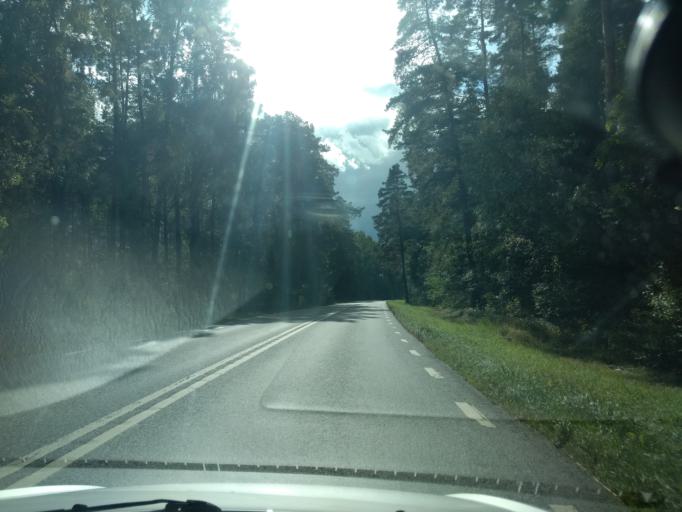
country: SE
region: Uppsala
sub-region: Uppsala Kommun
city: Saevja
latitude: 59.7718
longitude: 17.6558
